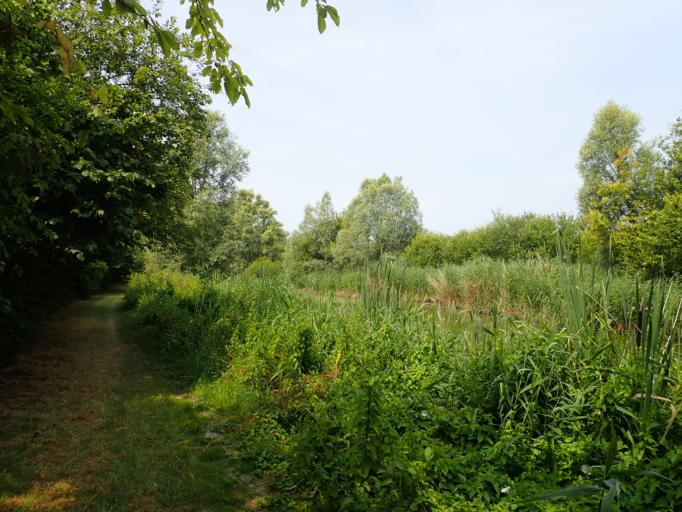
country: BE
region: Flanders
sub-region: Provincie Antwerpen
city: Kapellen
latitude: 51.2767
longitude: 4.3956
